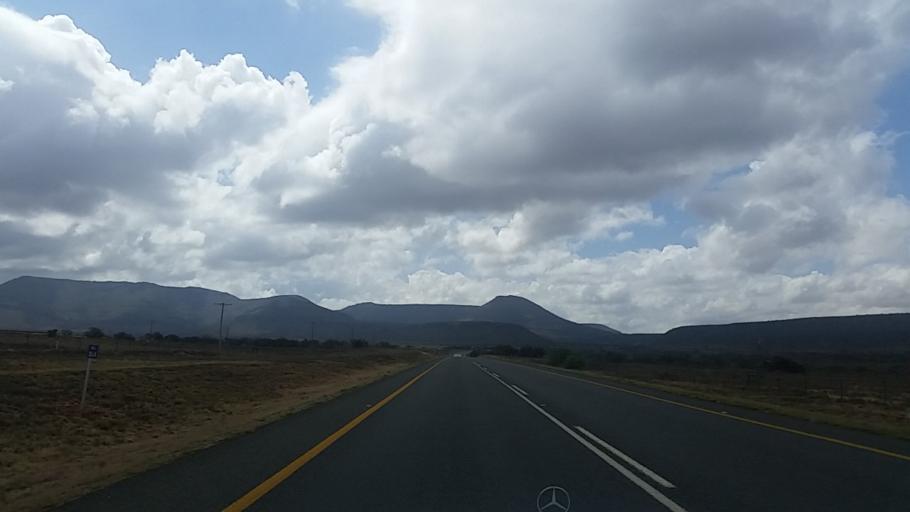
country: ZA
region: Eastern Cape
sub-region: Cacadu District Municipality
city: Graaff-Reinet
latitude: -32.0931
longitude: 24.6039
